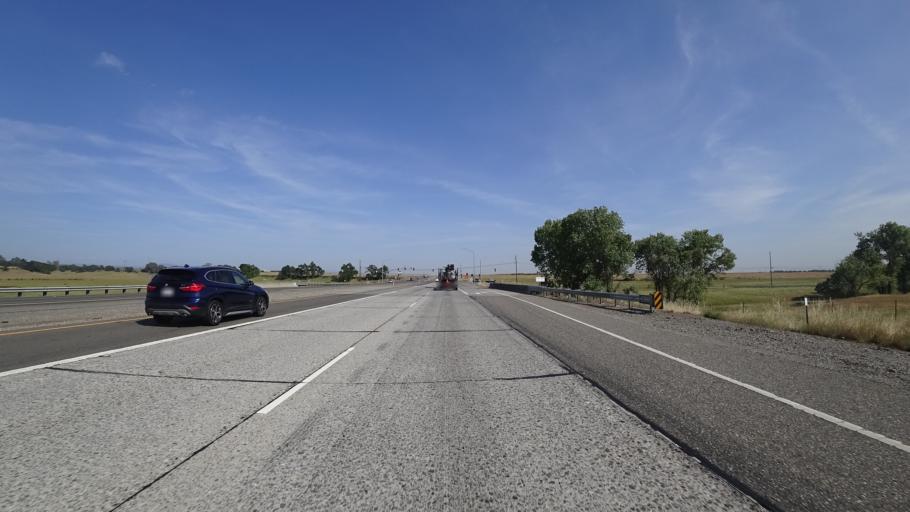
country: US
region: California
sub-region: Butte County
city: Durham
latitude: 39.6672
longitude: -121.7460
